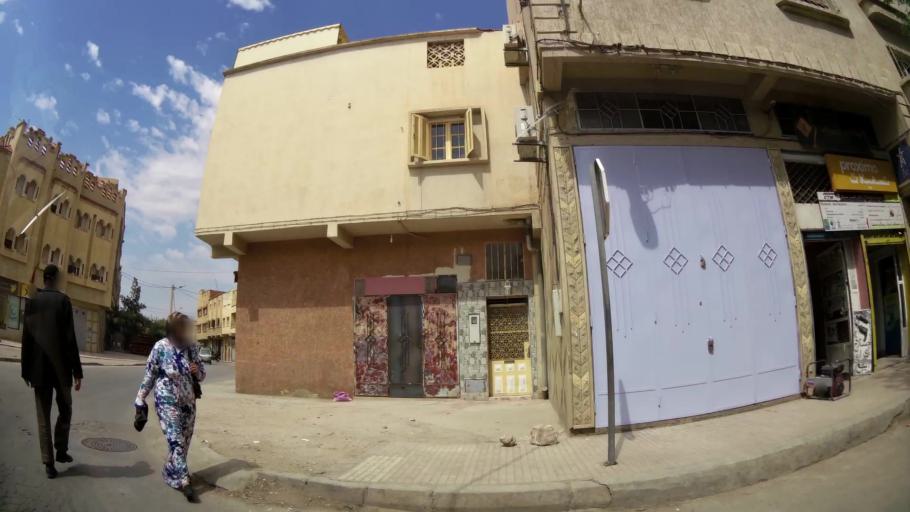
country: MA
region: Oriental
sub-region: Oujda-Angad
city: Oujda
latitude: 34.6845
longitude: -1.9029
